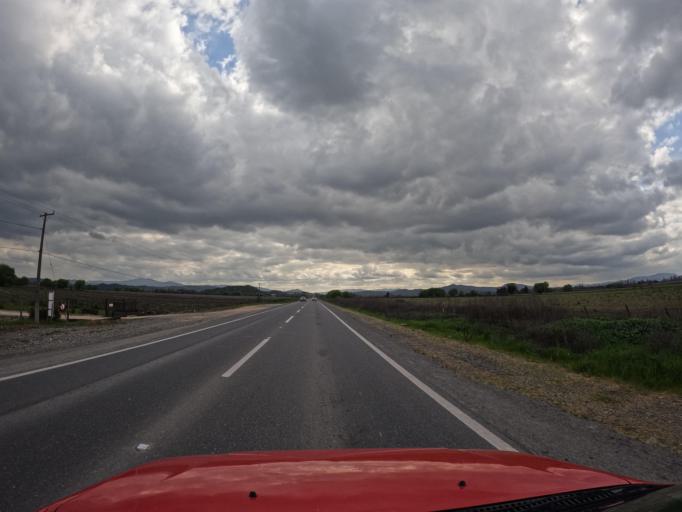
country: CL
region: Maule
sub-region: Provincia de Linares
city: San Javier
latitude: -35.6328
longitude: -71.7114
